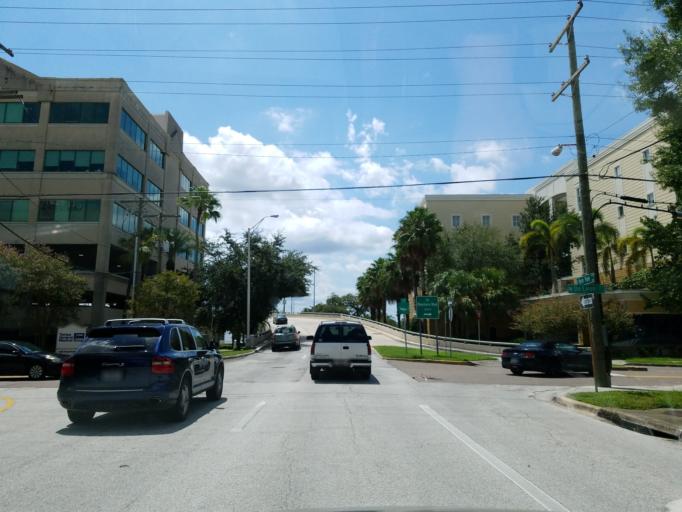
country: US
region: Florida
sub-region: Hillsborough County
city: Tampa
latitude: 27.9390
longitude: -82.4640
